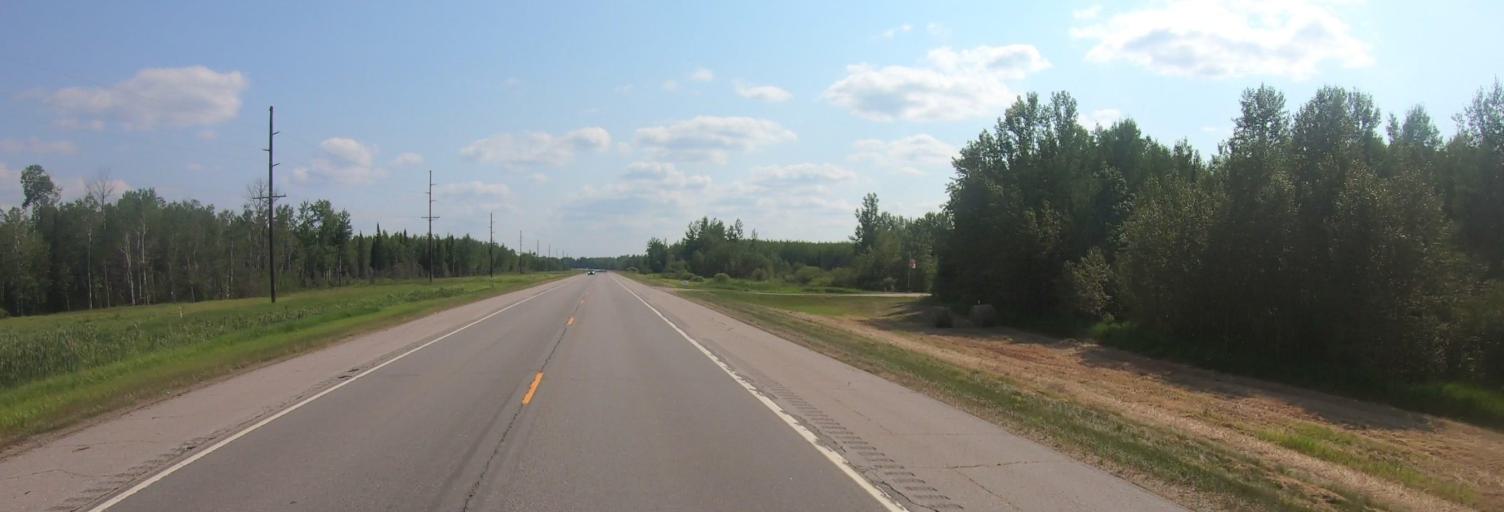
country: US
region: Minnesota
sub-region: Saint Louis County
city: Chisholm
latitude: 47.9409
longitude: -92.8303
